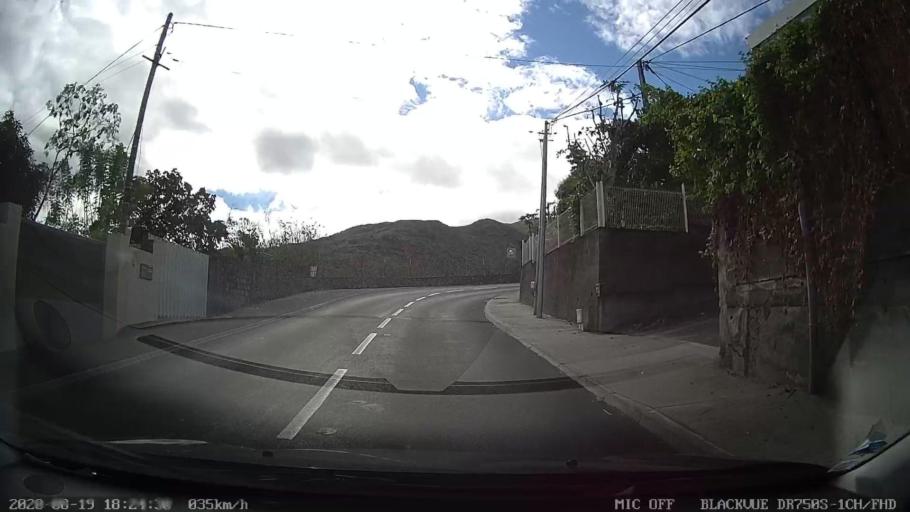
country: RE
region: Reunion
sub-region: Reunion
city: La Possession
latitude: -20.9513
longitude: 55.3460
